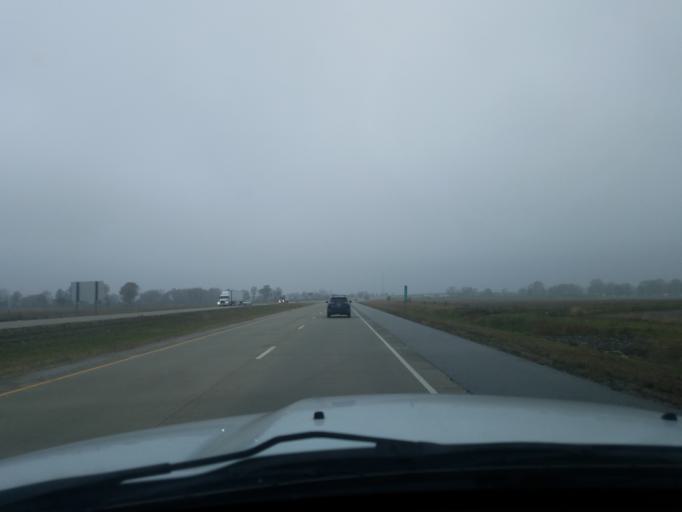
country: US
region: Indiana
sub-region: Howard County
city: Kokomo
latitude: 40.5362
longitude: -86.1164
